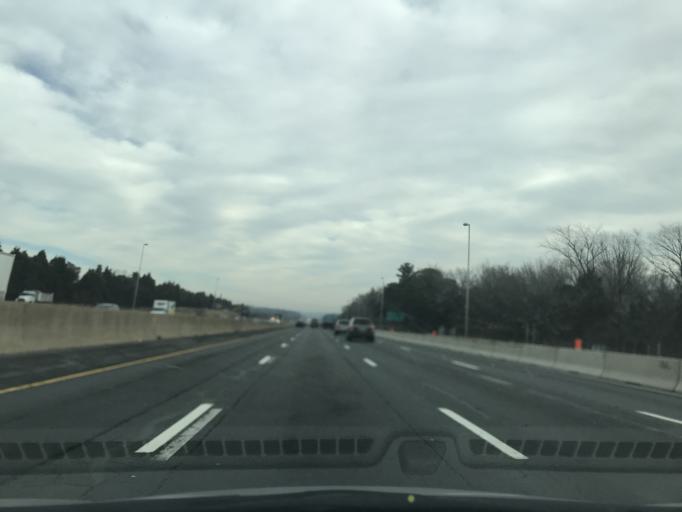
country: US
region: Virginia
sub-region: Prince William County
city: Sudley
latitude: 38.8035
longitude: -77.5064
